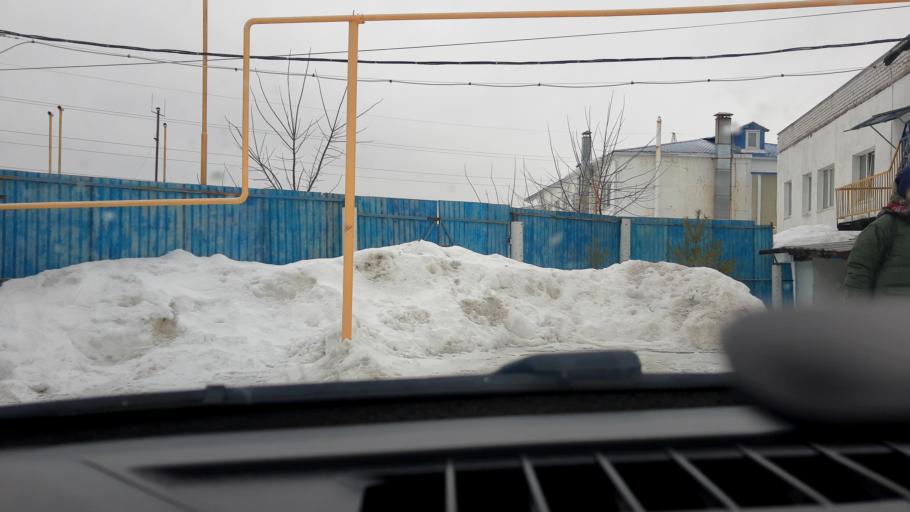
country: RU
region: Nizjnij Novgorod
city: Nizhniy Novgorod
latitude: 56.3345
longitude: 43.9089
